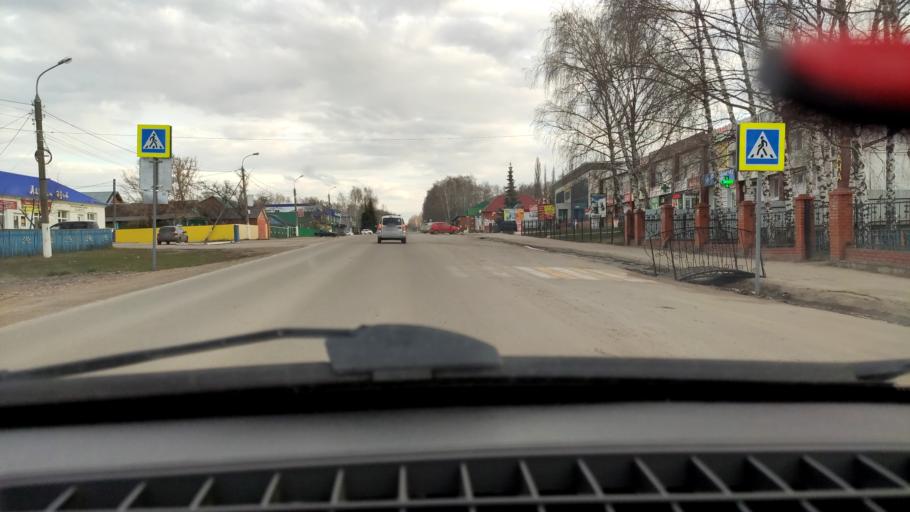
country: RU
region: Bashkortostan
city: Tolbazy
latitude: 54.0189
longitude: 55.8864
